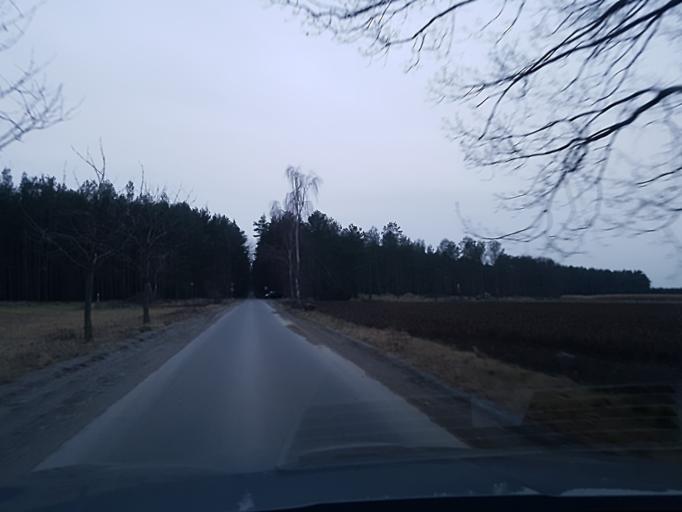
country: DE
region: Brandenburg
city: Schonewalde
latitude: 51.6555
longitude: 13.6286
